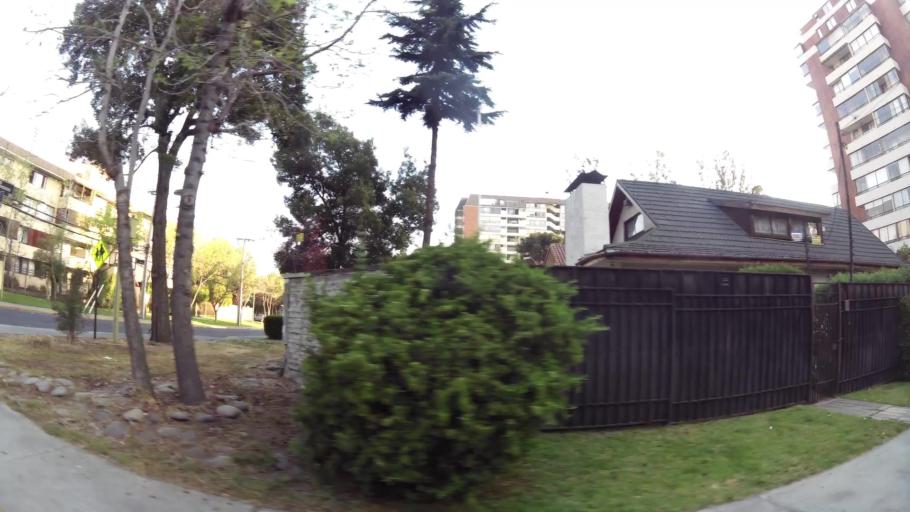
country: CL
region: Santiago Metropolitan
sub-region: Provincia de Santiago
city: Villa Presidente Frei, Nunoa, Santiago, Chile
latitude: -33.3937
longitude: -70.5539
